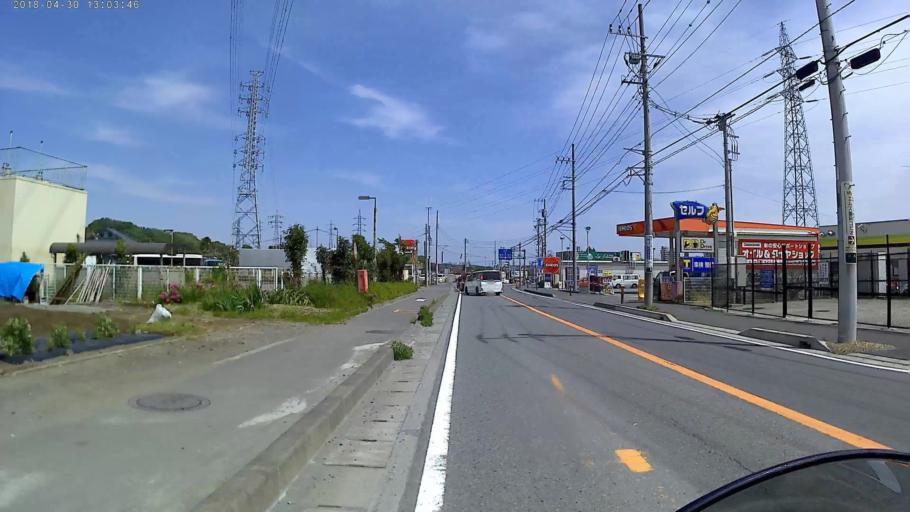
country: JP
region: Tokyo
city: Hachioji
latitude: 35.5901
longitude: 139.3076
